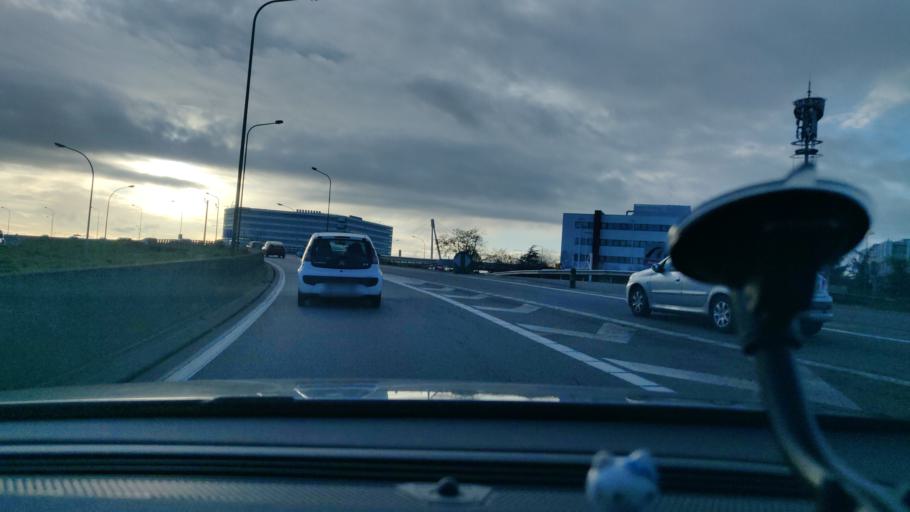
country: FR
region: Midi-Pyrenees
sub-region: Departement de la Haute-Garonne
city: Blagnac
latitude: 43.6095
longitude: 1.3711
